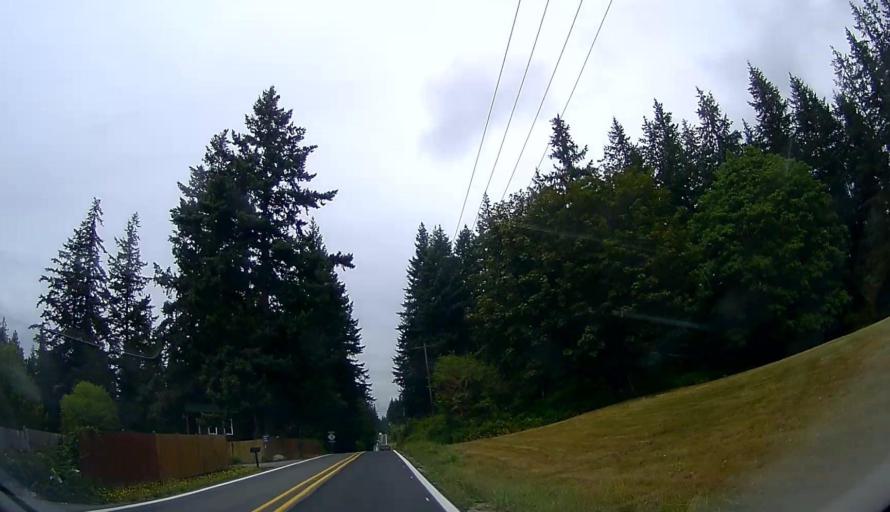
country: US
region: Washington
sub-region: Snohomish County
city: Warm Beach
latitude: 48.1603
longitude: -122.3576
